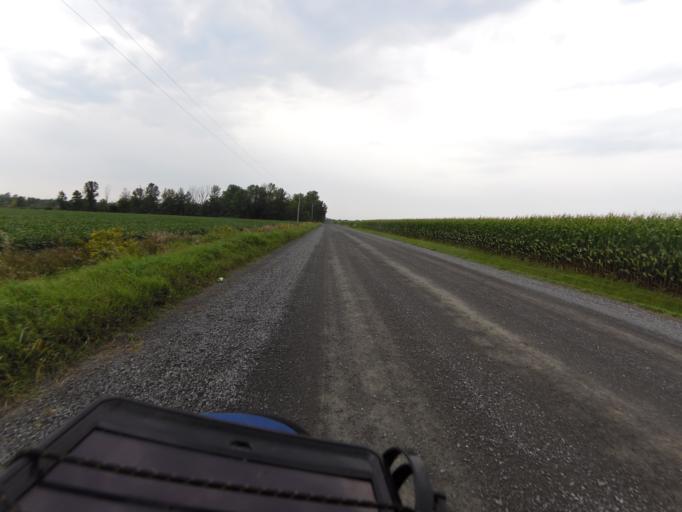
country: CA
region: Ontario
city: Ottawa
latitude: 45.1707
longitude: -75.4237
